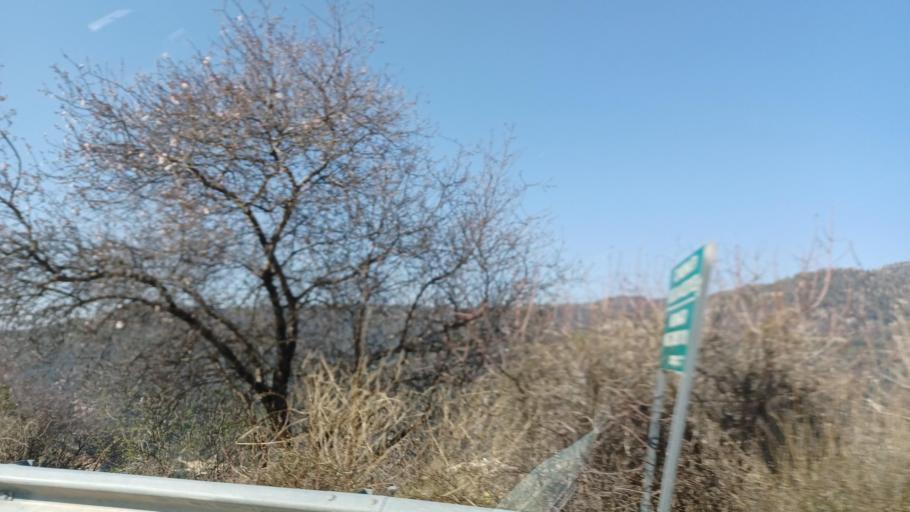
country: CY
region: Limassol
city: Sotira
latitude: 34.8038
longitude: 32.9156
